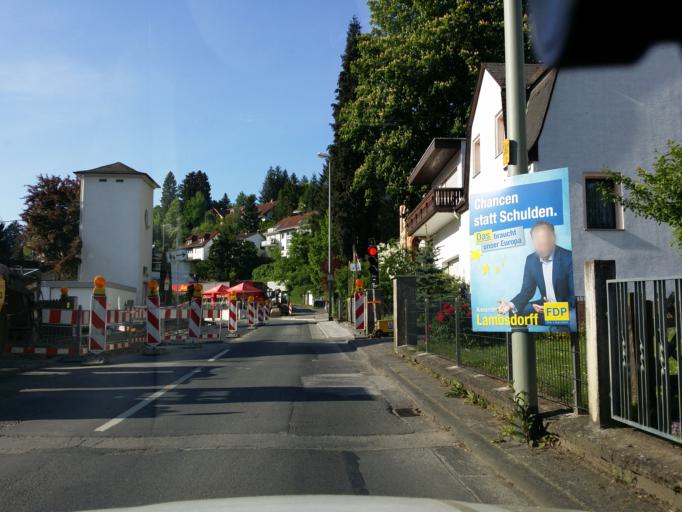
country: DE
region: Hesse
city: Eppstein
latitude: 50.1446
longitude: 8.3850
